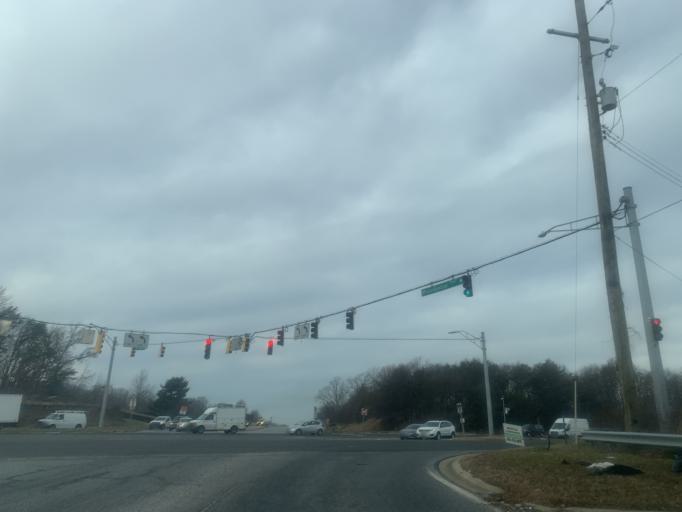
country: US
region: Maryland
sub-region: Prince George's County
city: Forestville
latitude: 38.8299
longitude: -76.8561
